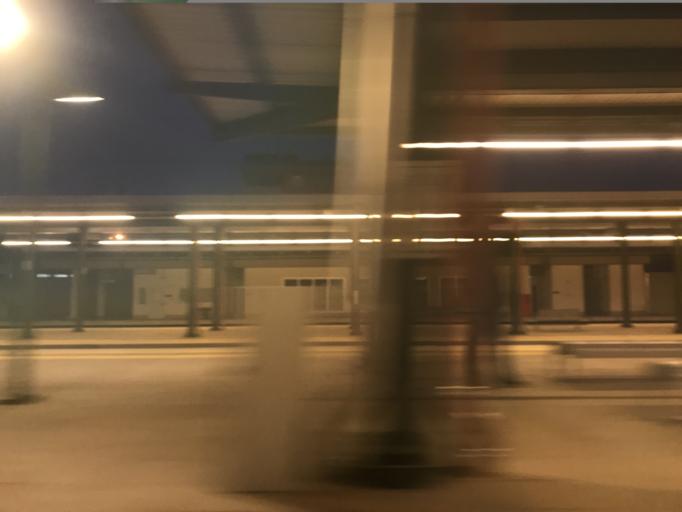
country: TR
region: Kocaeli
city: Darica
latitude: 40.7839
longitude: 29.4106
